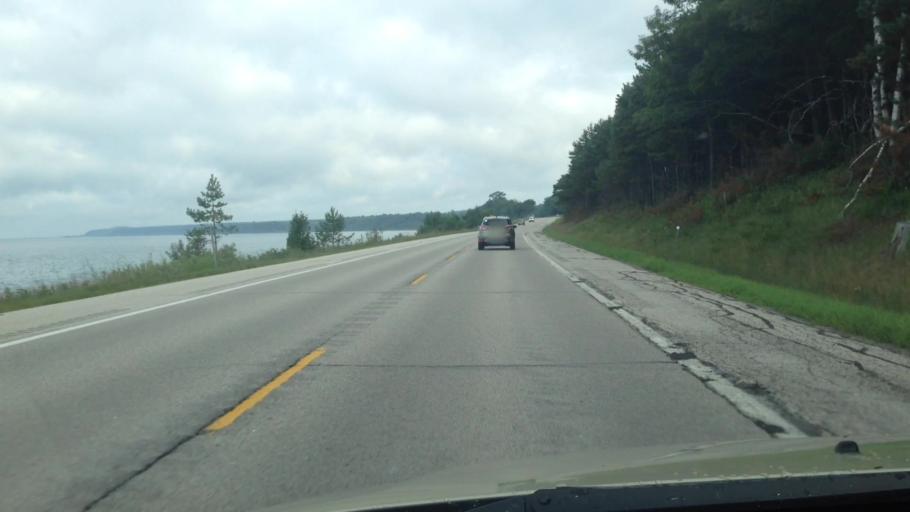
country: US
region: Michigan
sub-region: Mackinac County
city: Saint Ignace
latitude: 45.9973
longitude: -84.9902
